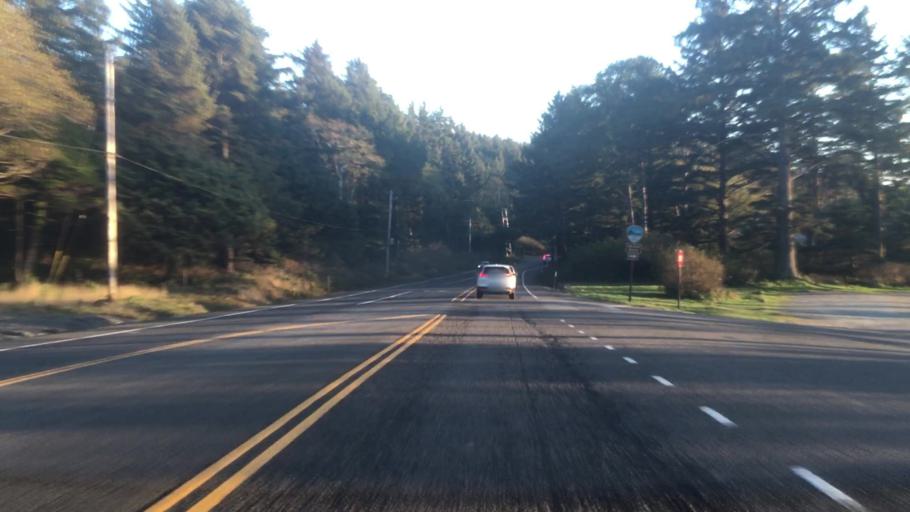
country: US
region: Oregon
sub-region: Clatsop County
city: Cannon Beach
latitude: 45.8468
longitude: -123.9601
